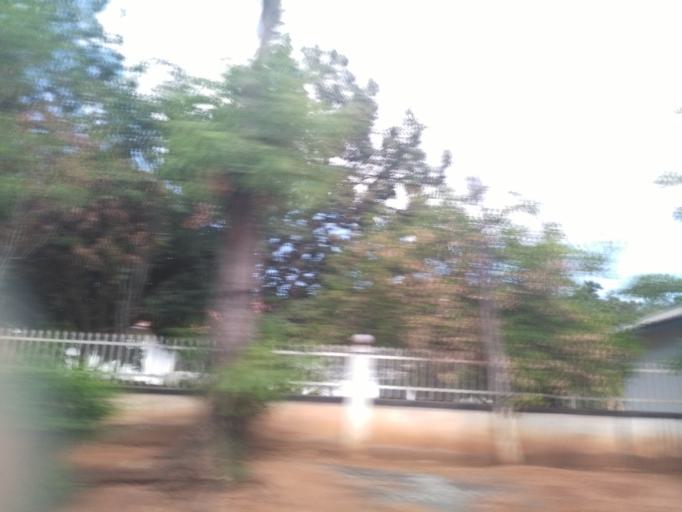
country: TZ
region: Mwanza
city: Mwanza
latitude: -2.5092
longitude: 32.9095
